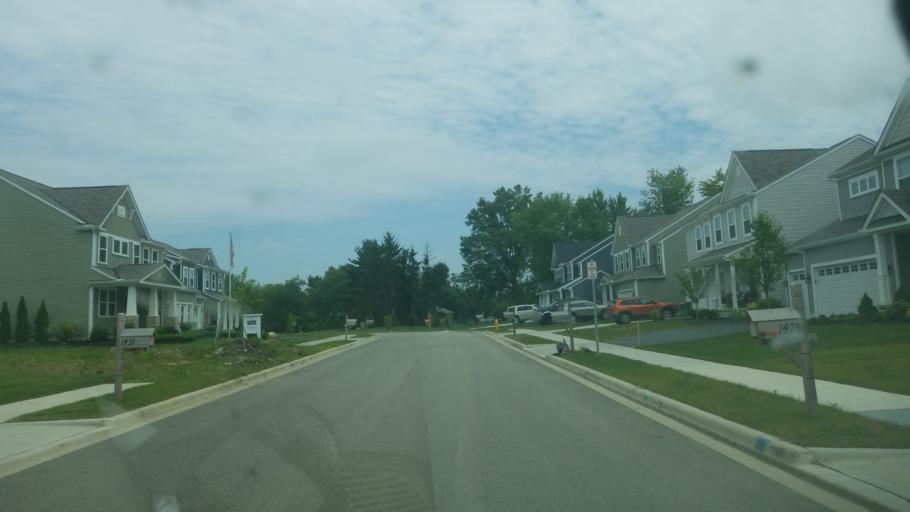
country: US
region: Ohio
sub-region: Franklin County
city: Reynoldsburg
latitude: 40.0167
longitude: -82.7751
